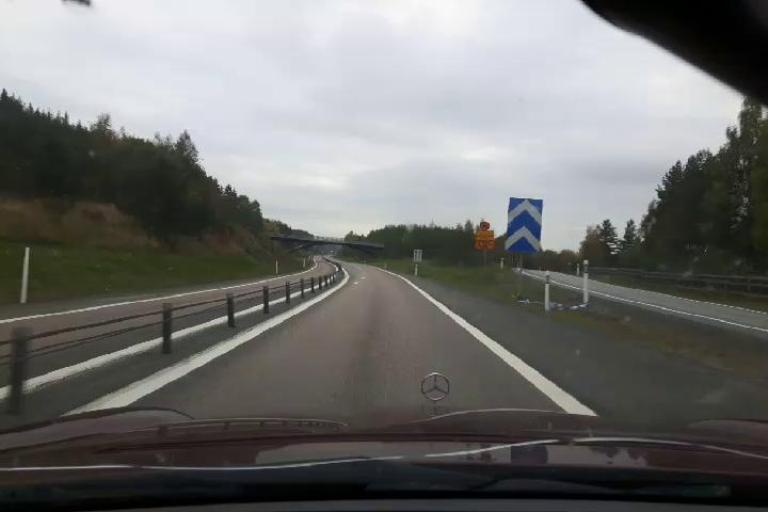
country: SE
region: Vaesternorrland
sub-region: Kramfors Kommun
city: Nordingra
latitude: 62.9316
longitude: 18.0958
